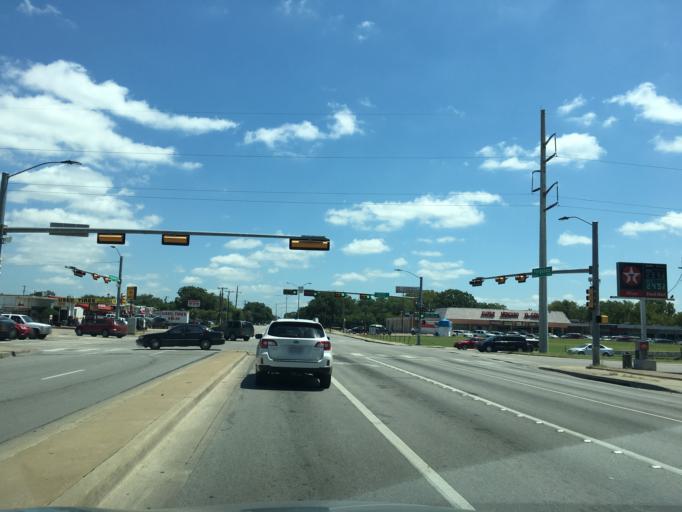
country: US
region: Texas
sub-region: Dallas County
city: Garland
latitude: 32.8421
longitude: -96.6651
